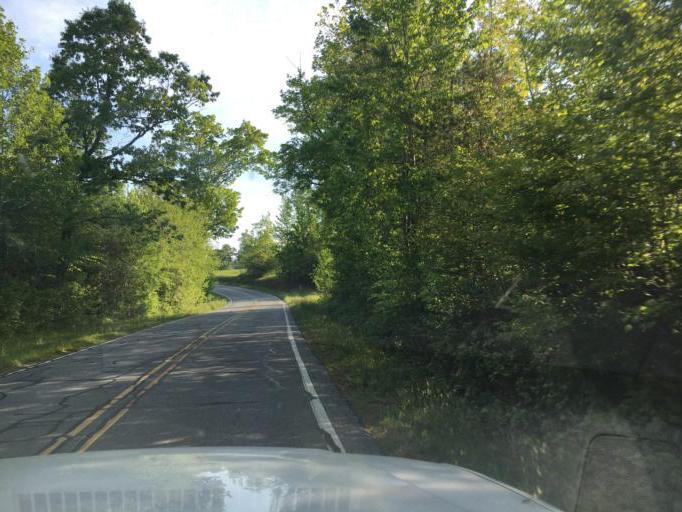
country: US
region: North Carolina
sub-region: Rutherford County
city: Rutherfordton
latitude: 35.3243
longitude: -81.9903
